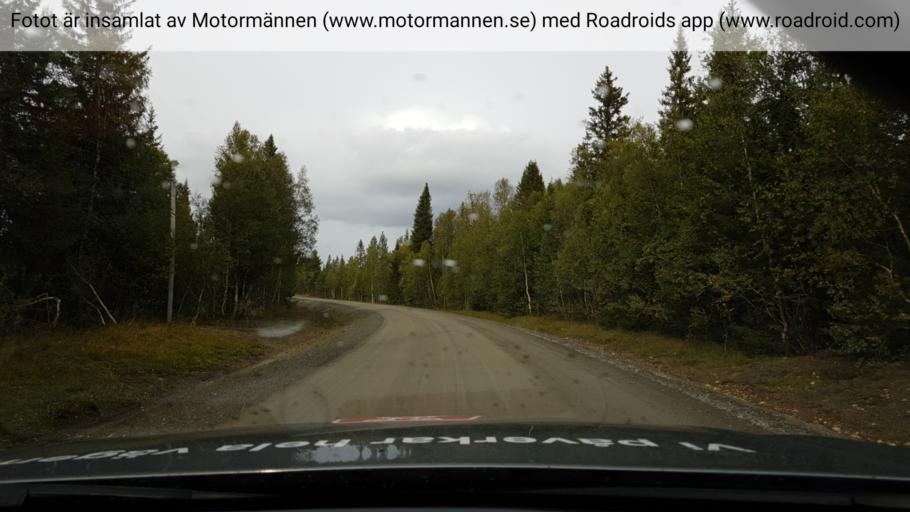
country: NO
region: Nord-Trondelag
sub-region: Snasa
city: Snaase
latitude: 63.7274
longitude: 12.4758
